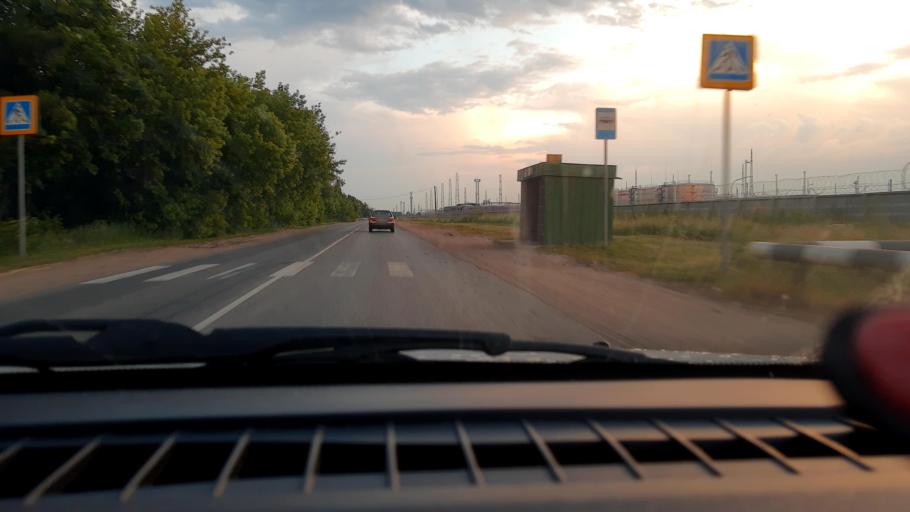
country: RU
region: Nizjnij Novgorod
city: Kstovo
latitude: 56.1242
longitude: 44.1277
